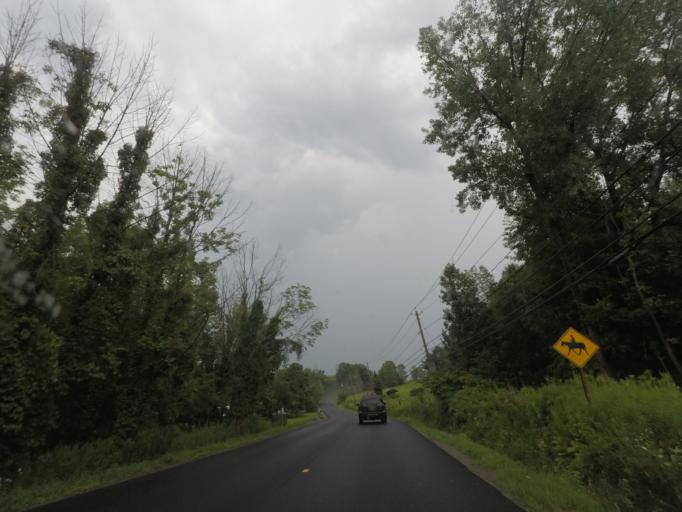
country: US
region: New York
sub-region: Rensselaer County
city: Poestenkill
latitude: 42.6892
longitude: -73.5456
